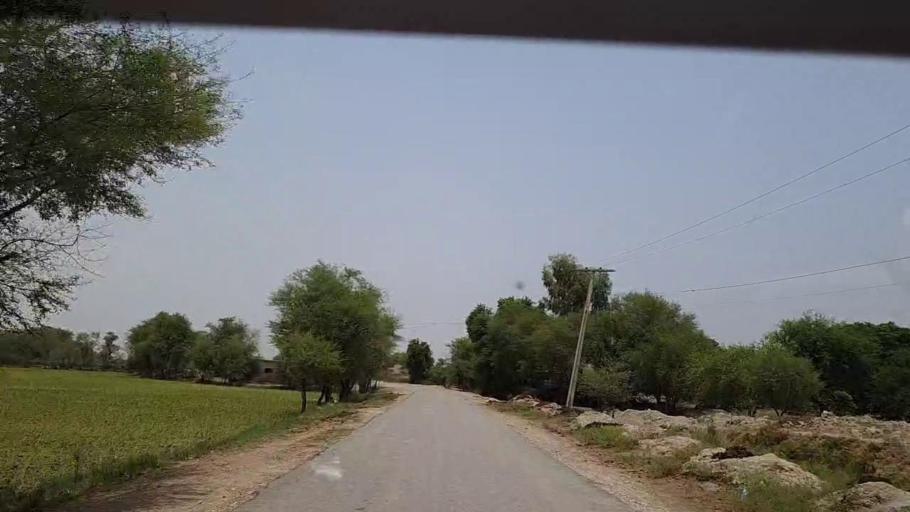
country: PK
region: Sindh
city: Khairpur Nathan Shah
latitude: 27.0212
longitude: 67.6693
